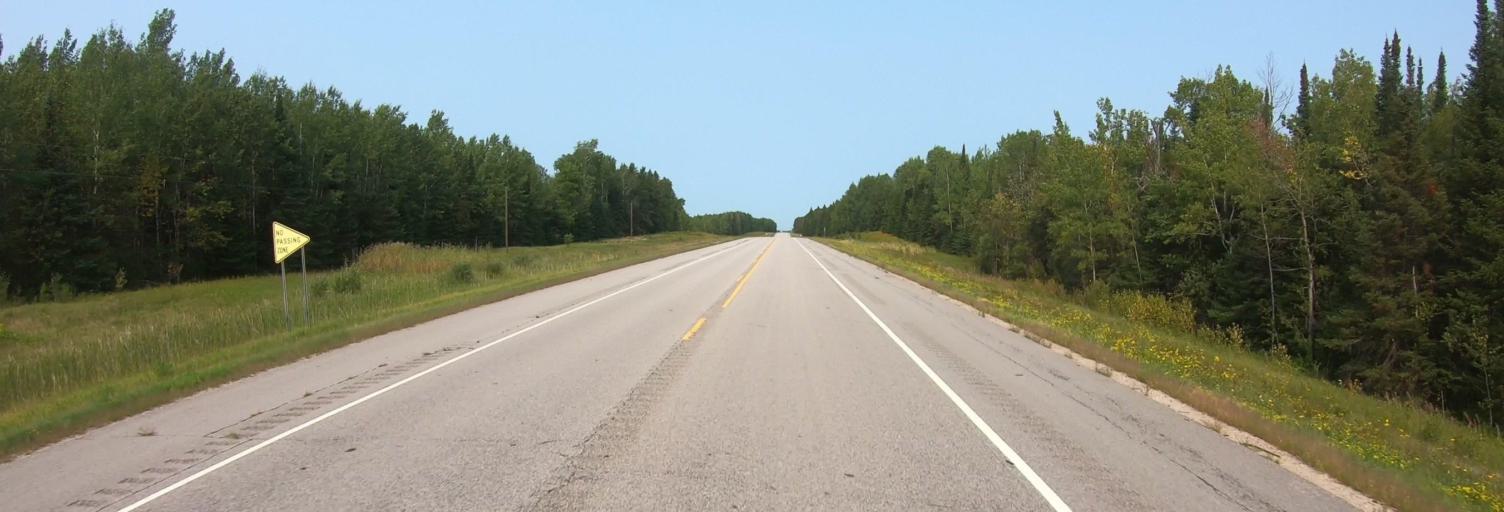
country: CA
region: Ontario
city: Fort Frances
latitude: 48.3720
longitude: -92.9742
